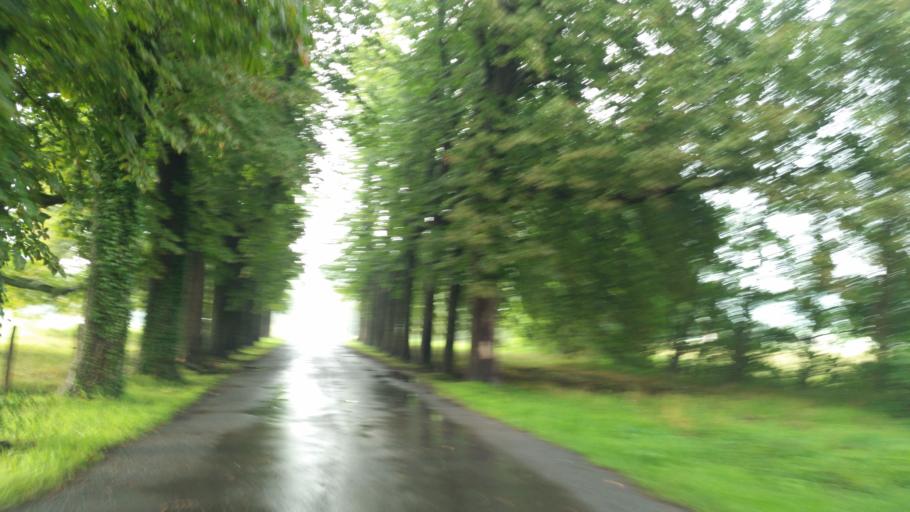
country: BE
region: Wallonia
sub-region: Province du Luxembourg
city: Tellin
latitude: 50.1229
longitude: 5.1944
